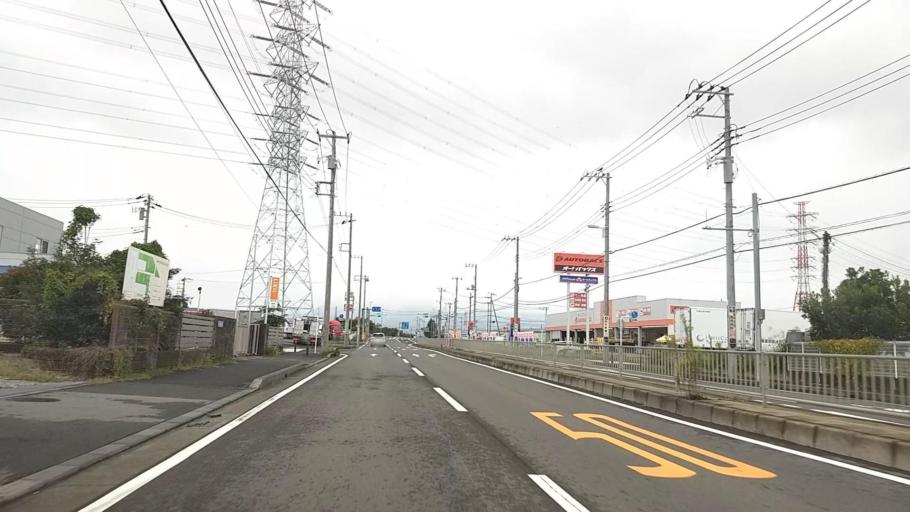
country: JP
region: Kanagawa
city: Isehara
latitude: 35.4016
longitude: 139.3414
